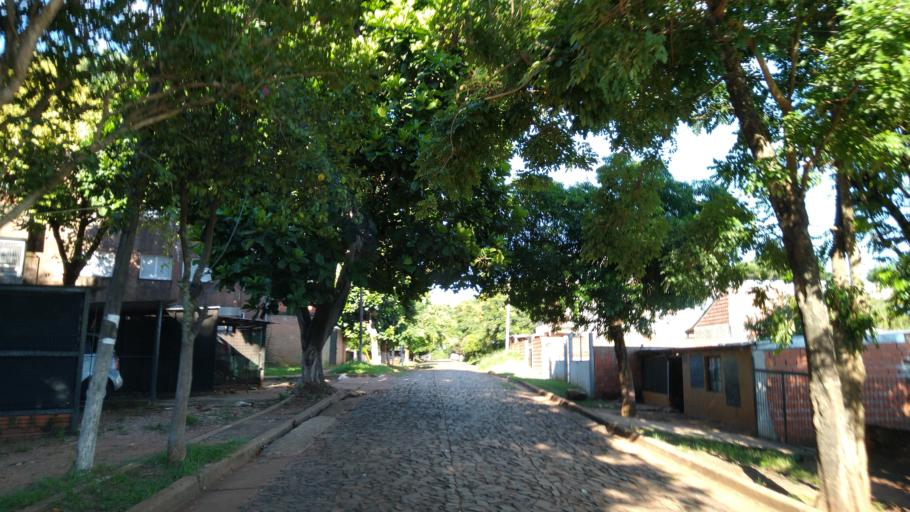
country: AR
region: Misiones
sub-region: Departamento de Capital
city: Posadas
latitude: -27.3588
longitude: -55.9314
